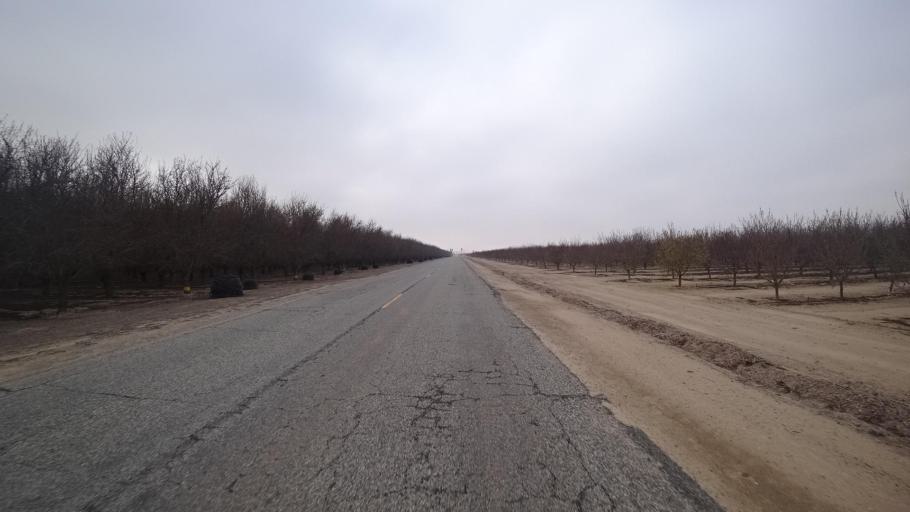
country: US
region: California
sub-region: Kern County
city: Maricopa
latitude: 35.1231
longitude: -119.3517
